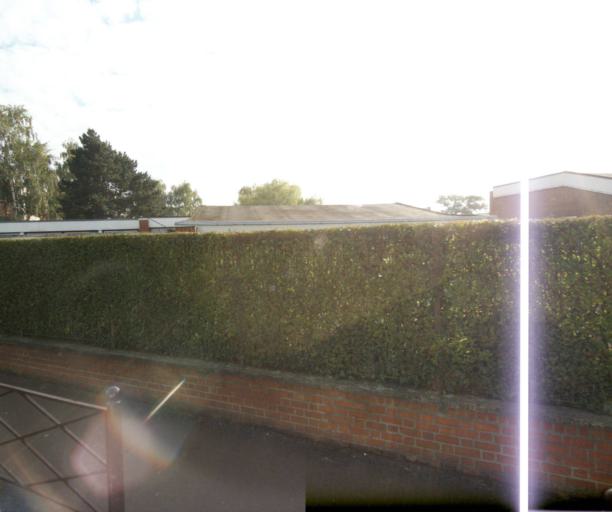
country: FR
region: Nord-Pas-de-Calais
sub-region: Departement du Nord
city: Wattignies
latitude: 50.5858
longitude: 3.0372
